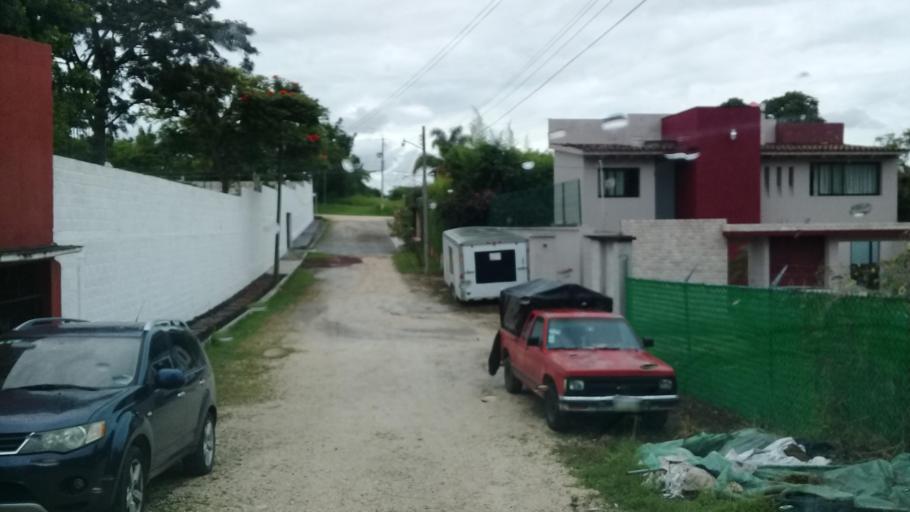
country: MX
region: Veracruz
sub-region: Emiliano Zapata
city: Jacarandas
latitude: 19.5051
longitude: -96.8393
